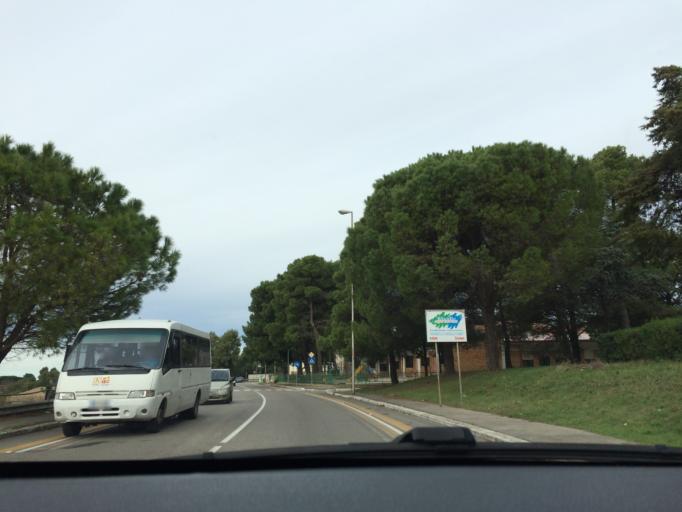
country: IT
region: Basilicate
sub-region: Provincia di Matera
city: Matera
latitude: 40.6581
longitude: 16.6049
